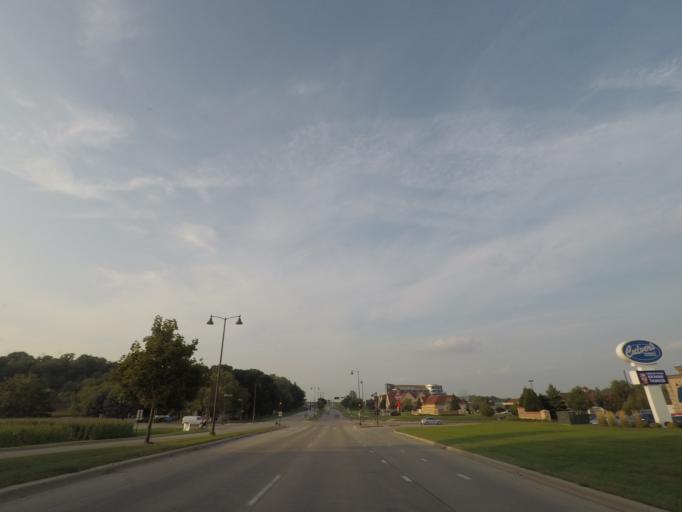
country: US
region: Wisconsin
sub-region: Dane County
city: Cottage Grove
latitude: 43.1042
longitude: -89.1992
